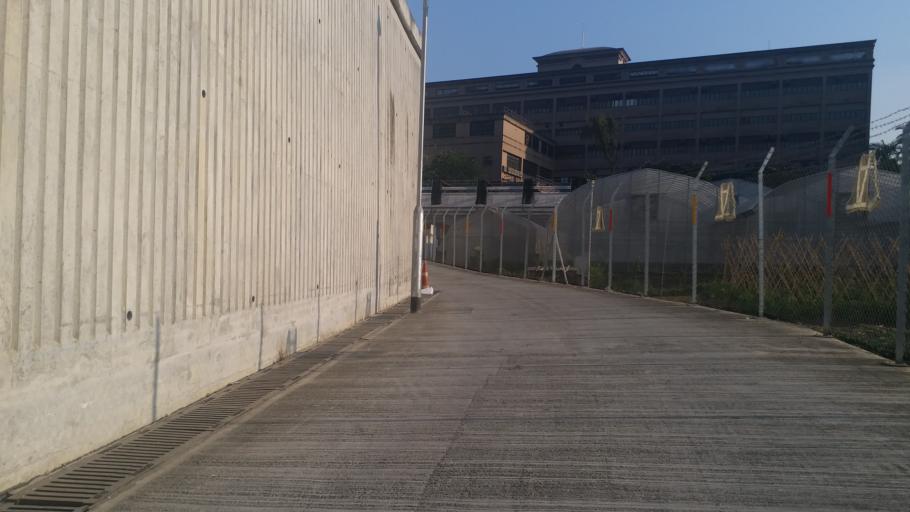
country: HK
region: Tuen Mun
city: Tuen Mun
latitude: 22.4109
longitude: 113.9720
